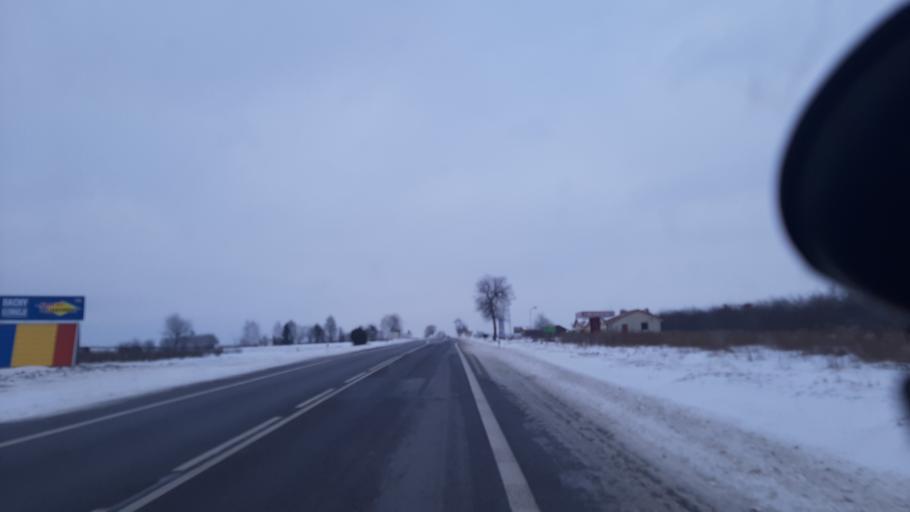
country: PL
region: Lublin Voivodeship
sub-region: Powiat pulawski
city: Markuszow
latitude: 51.3827
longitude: 22.2242
